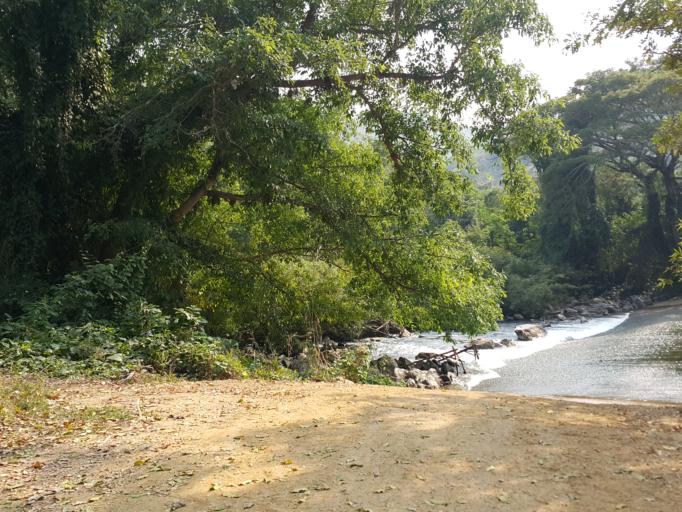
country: TH
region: Sukhothai
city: Thung Saliam
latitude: 17.3309
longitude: 99.4792
